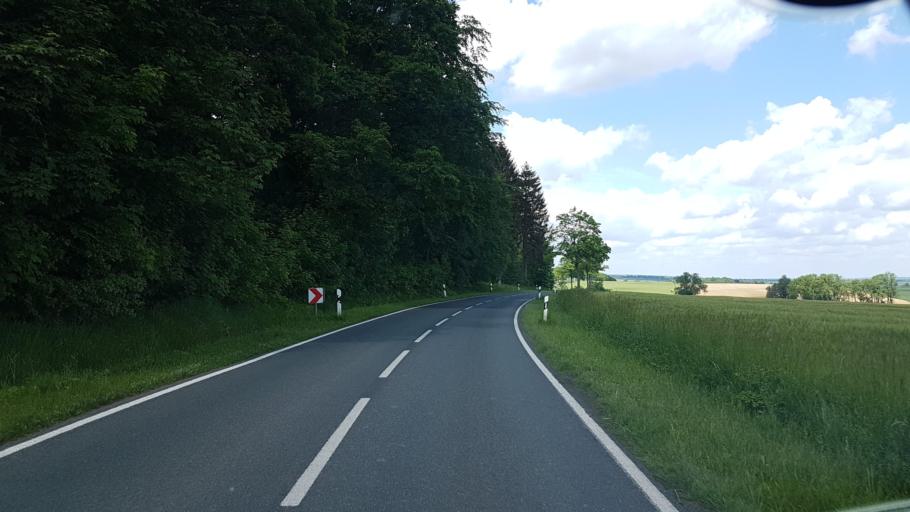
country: DE
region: Lower Saxony
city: Warberg
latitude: 52.1806
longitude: 10.8982
